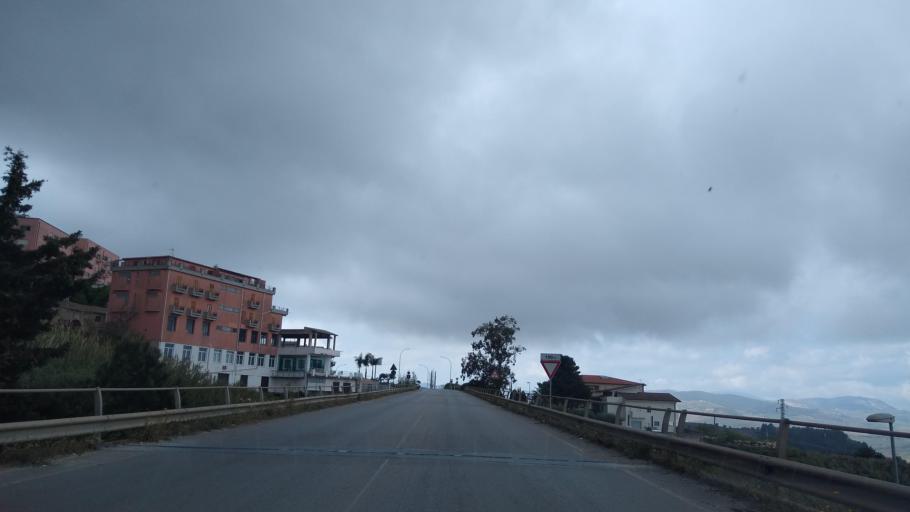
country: IT
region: Sicily
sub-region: Trapani
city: Alcamo
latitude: 37.9818
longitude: 12.9486
